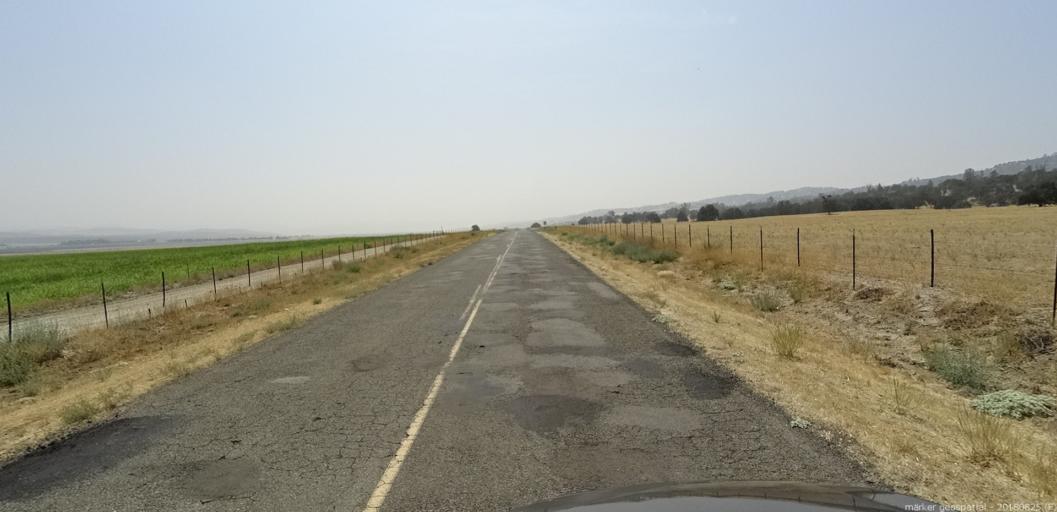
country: US
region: California
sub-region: San Luis Obispo County
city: Shandon
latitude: 35.8154
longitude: -120.3770
